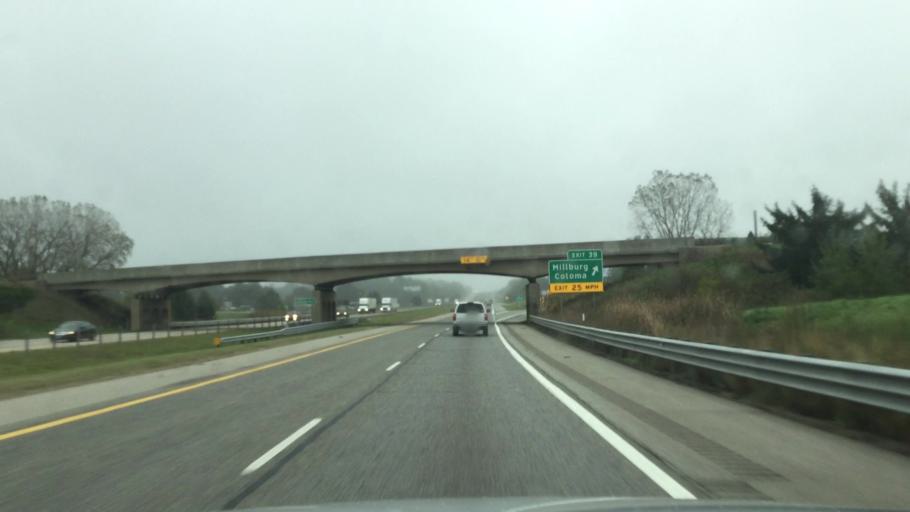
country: US
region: Michigan
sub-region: Berrien County
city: Coloma
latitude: 42.1756
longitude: -86.3062
